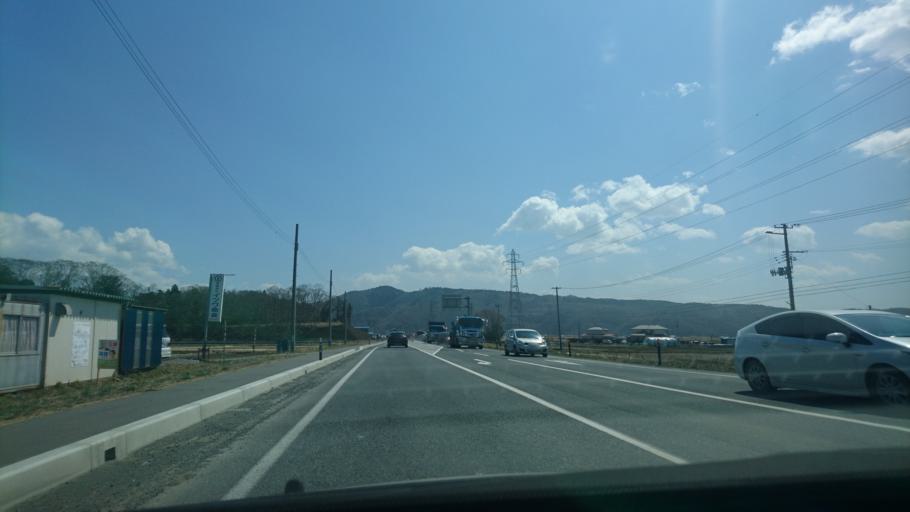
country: JP
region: Miyagi
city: Ishinomaki
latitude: 38.4525
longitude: 141.3129
